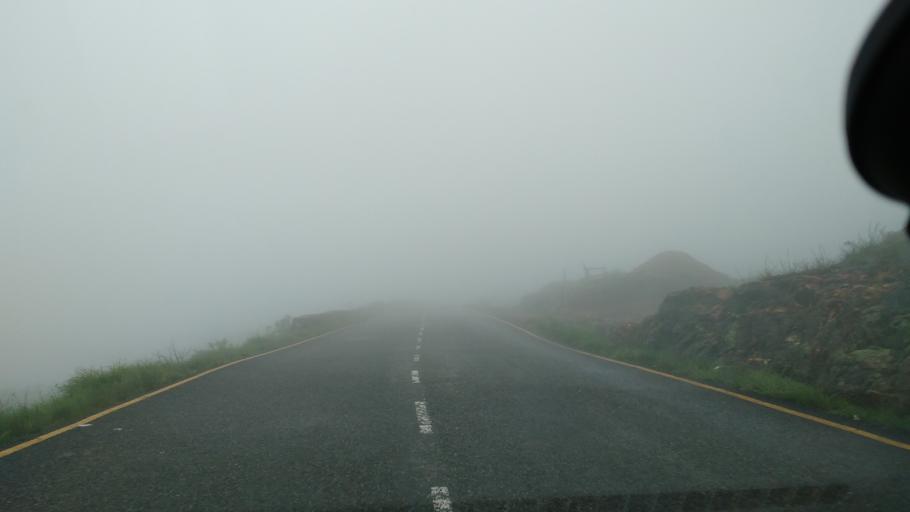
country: IN
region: Meghalaya
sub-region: East Khasi Hills
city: Cherrapunji
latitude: 25.3096
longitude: 91.7284
